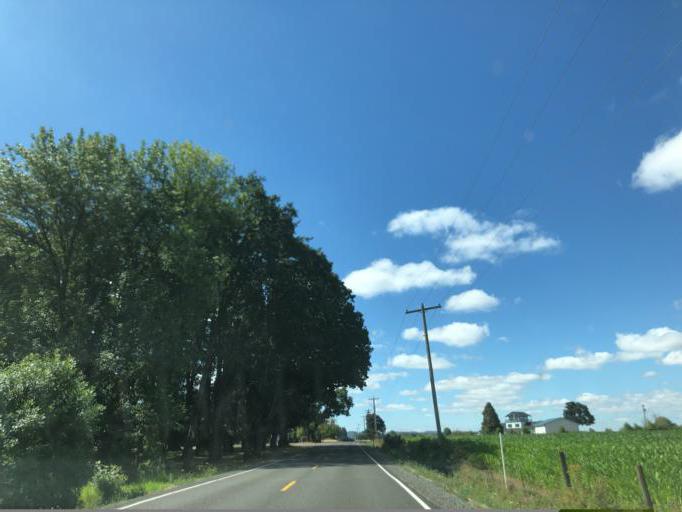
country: US
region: Oregon
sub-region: Marion County
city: Mount Angel
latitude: 45.0730
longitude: -122.7435
